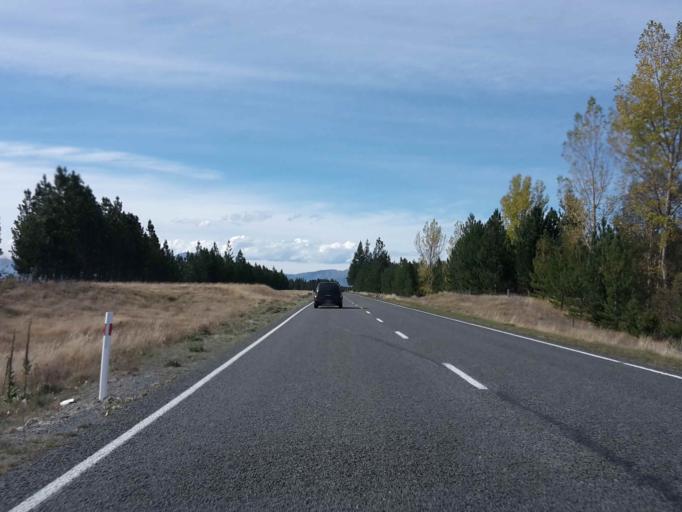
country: NZ
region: Canterbury
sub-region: Timaru District
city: Pleasant Point
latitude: -44.1869
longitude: 170.3030
